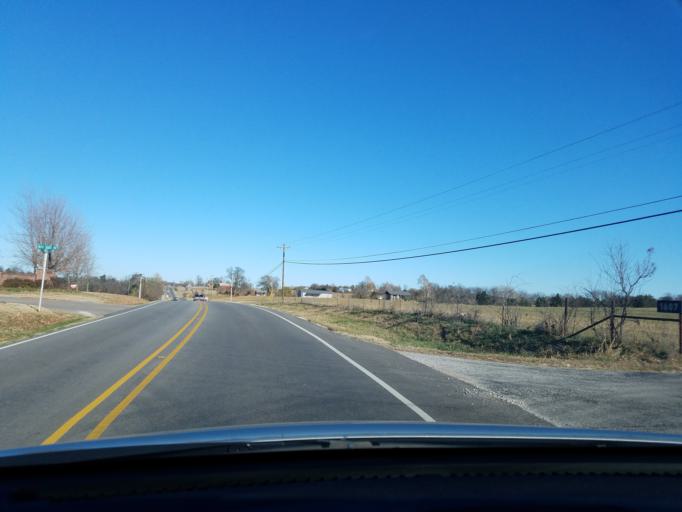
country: US
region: Arkansas
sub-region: Carroll County
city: Berryville
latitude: 36.3855
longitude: -93.5665
